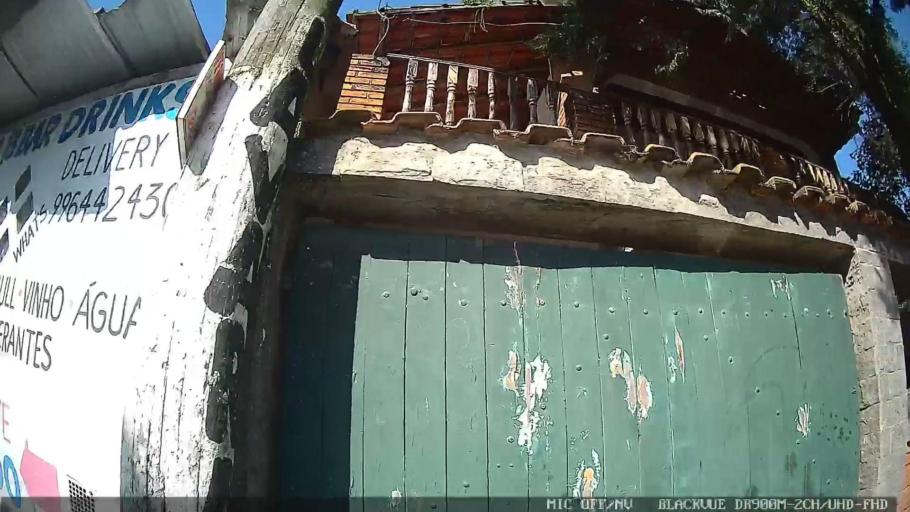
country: BR
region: Sao Paulo
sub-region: Guaruja
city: Guaruja
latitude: -23.9961
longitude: -46.3017
